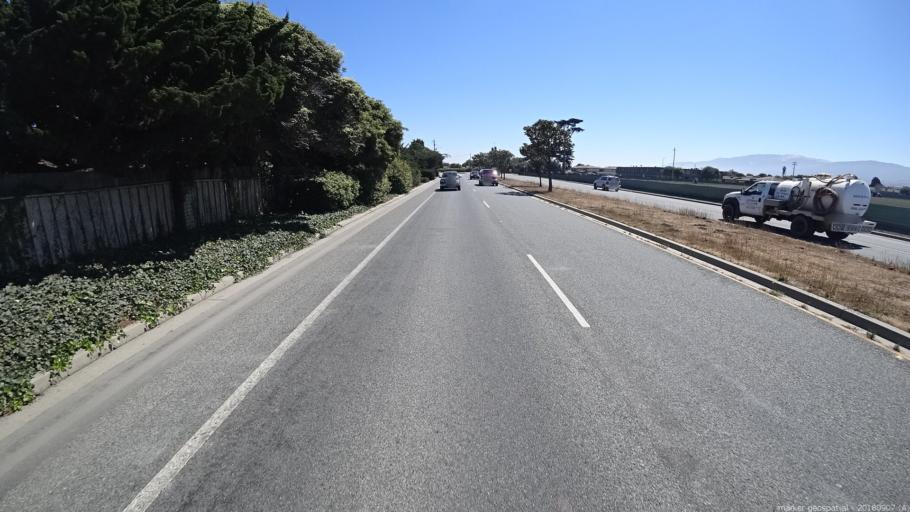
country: US
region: California
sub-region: Monterey County
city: Salinas
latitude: 36.6628
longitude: -121.6745
